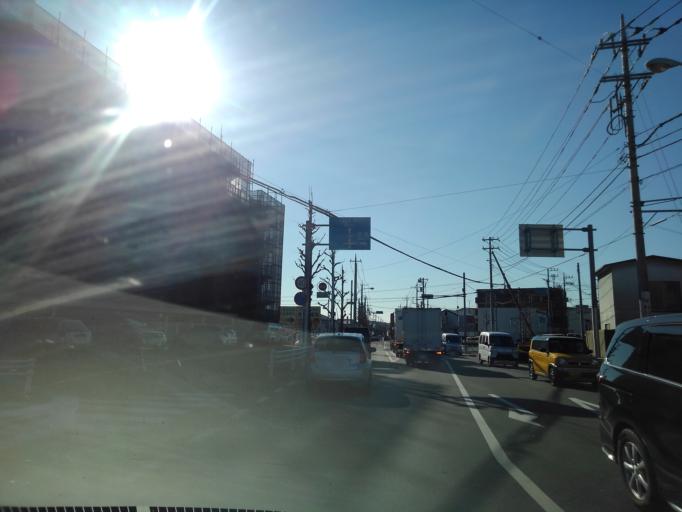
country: JP
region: Tokyo
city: Hino
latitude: 35.7266
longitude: 139.3828
